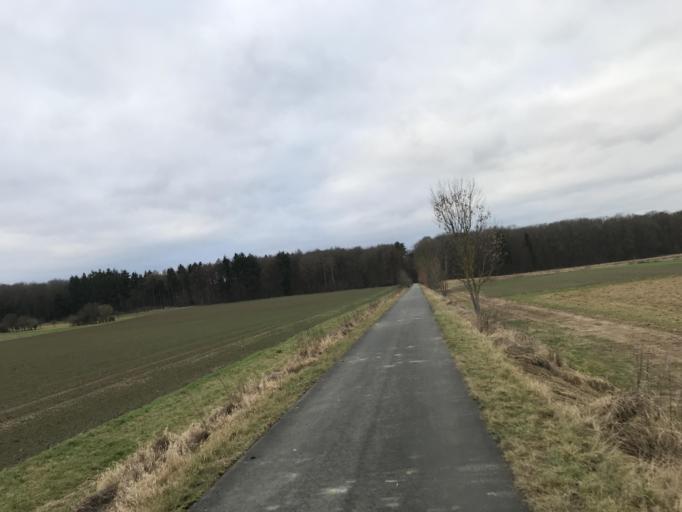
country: DE
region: Hesse
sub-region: Regierungsbezirk Darmstadt
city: Butzbach
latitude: 50.4575
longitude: 8.6329
